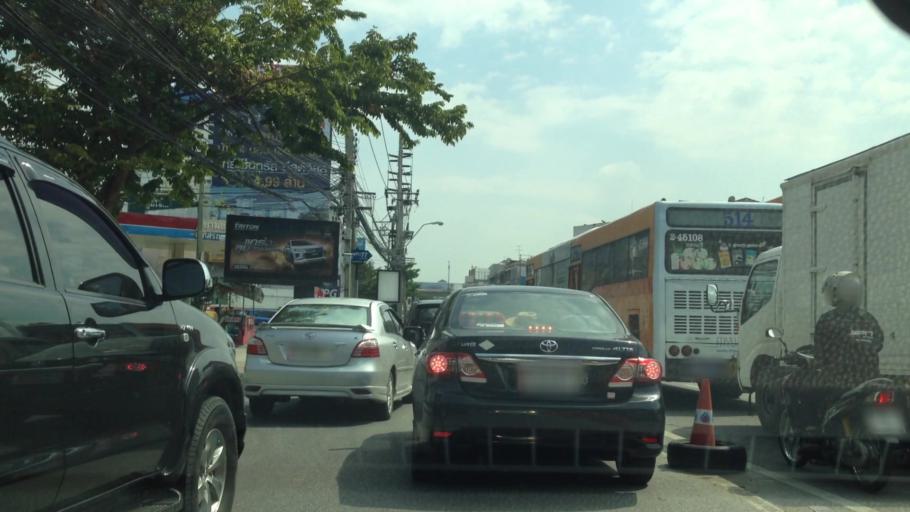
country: TH
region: Bangkok
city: Wang Thonglang
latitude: 13.7862
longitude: 100.6094
